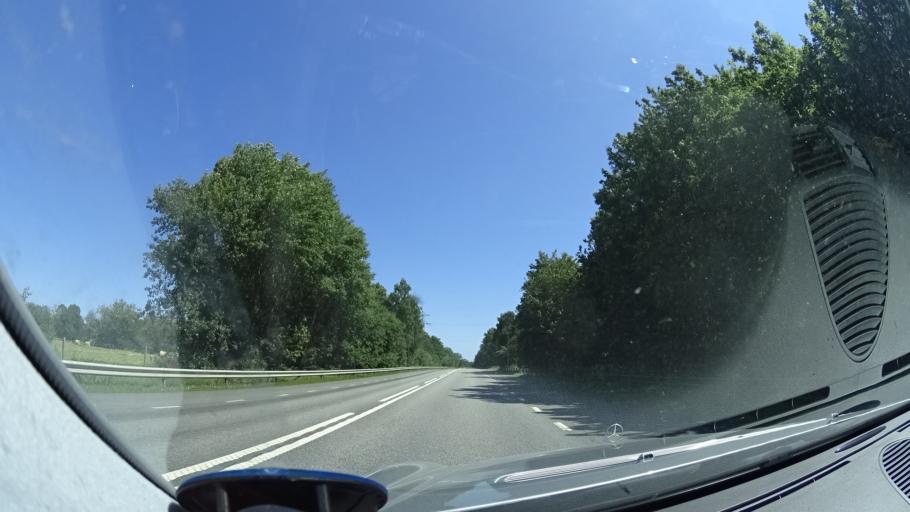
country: SE
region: Skane
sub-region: Hassleholms Kommun
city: Vinslov
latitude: 55.9462
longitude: 13.8781
